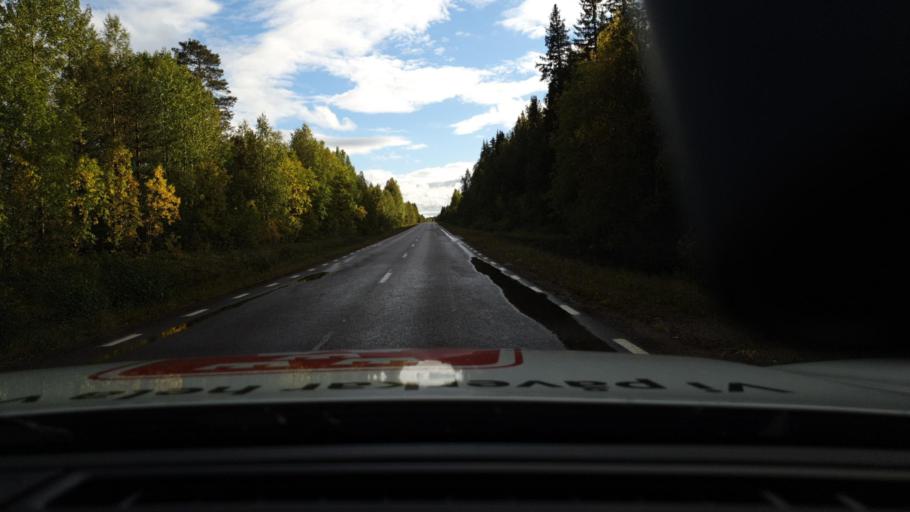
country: SE
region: Norrbotten
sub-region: Overkalix Kommun
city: OEverkalix
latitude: 66.8044
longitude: 22.7345
